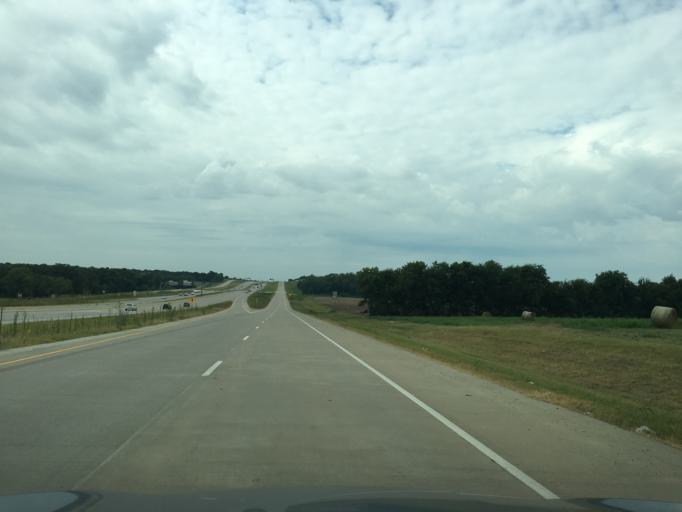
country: US
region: Texas
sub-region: Collin County
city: Melissa
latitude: 33.3063
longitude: -96.5917
